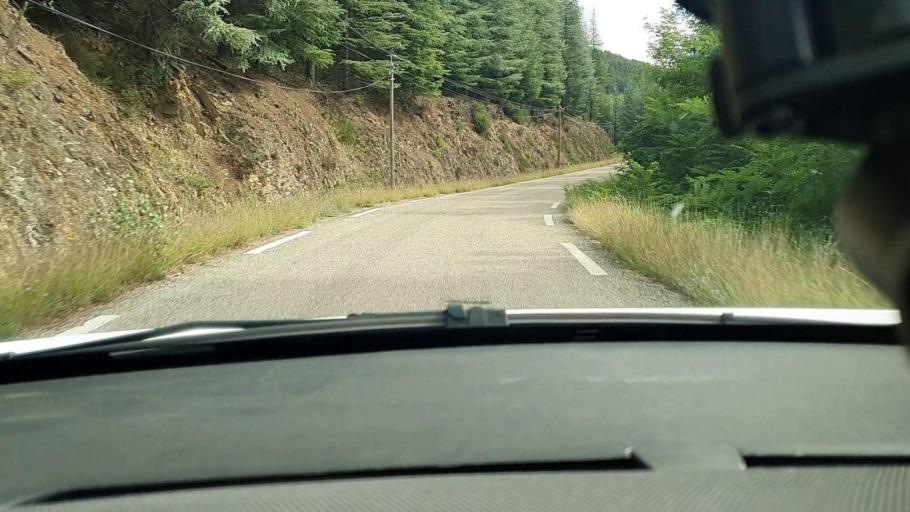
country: FR
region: Languedoc-Roussillon
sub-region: Departement du Gard
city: Branoux-les-Taillades
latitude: 44.3214
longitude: 3.9798
